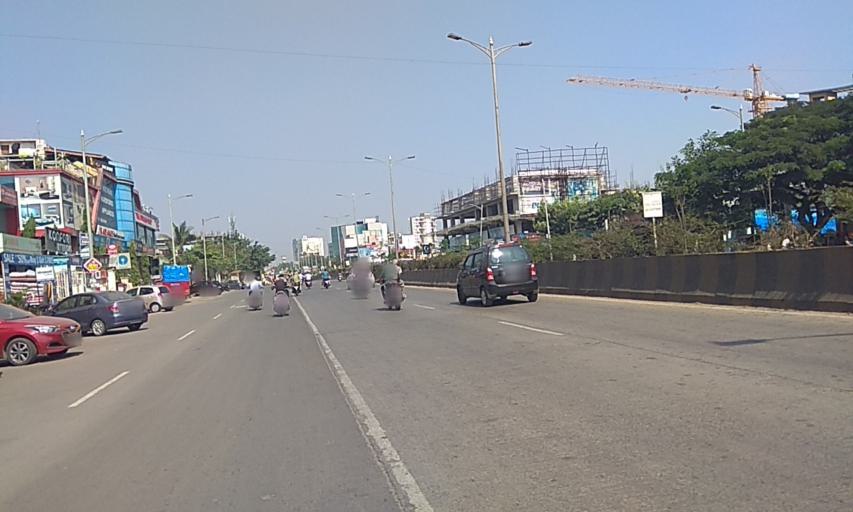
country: IN
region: Maharashtra
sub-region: Pune Division
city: Lohogaon
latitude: 18.5475
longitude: 73.9363
